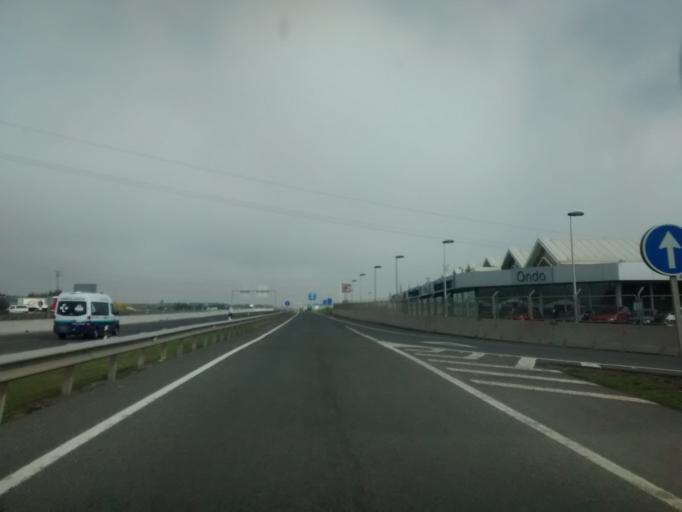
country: ES
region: Basque Country
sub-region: Provincia de Alava
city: Gasteiz / Vitoria
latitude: 42.8824
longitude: -2.6553
